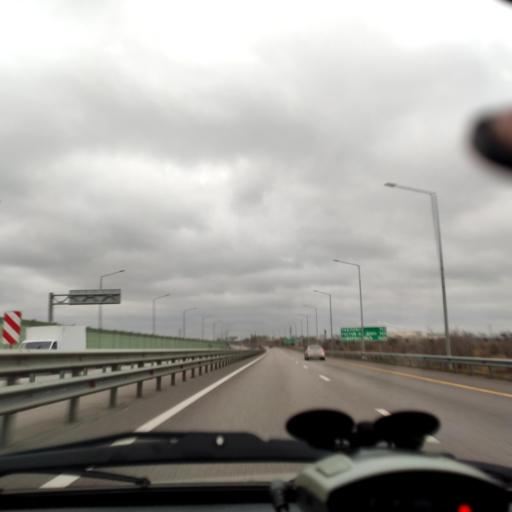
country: RU
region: Voronezj
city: Novaya Usman'
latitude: 51.6369
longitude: 39.3171
